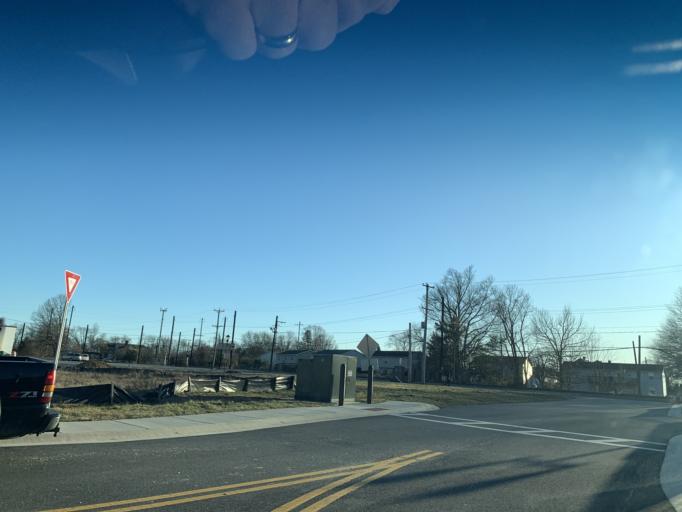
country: US
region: Maryland
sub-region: Cecil County
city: Perryville
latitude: 39.5607
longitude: -76.0735
